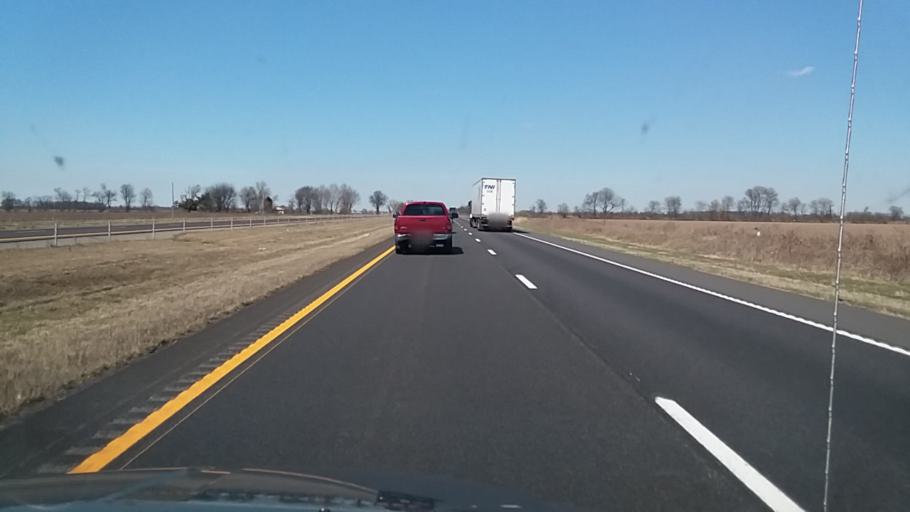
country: US
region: Missouri
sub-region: New Madrid County
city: New Madrid
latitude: 36.7257
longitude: -89.5378
